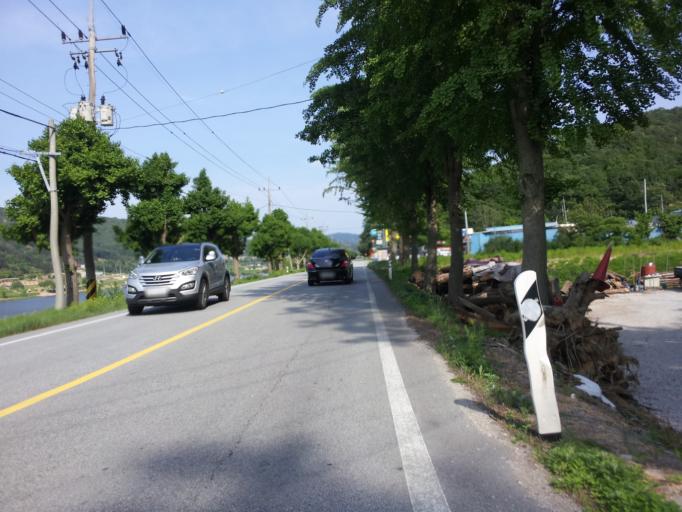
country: KR
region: Chungcheongnam-do
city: Gongju
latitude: 36.4450
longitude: 127.1822
